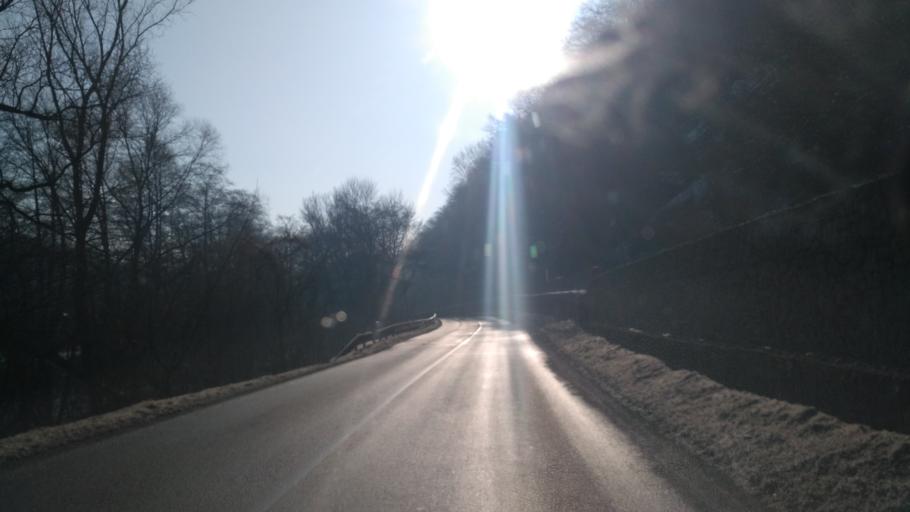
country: SK
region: Kosicky
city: Kosice
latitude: 48.7665
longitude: 21.2395
